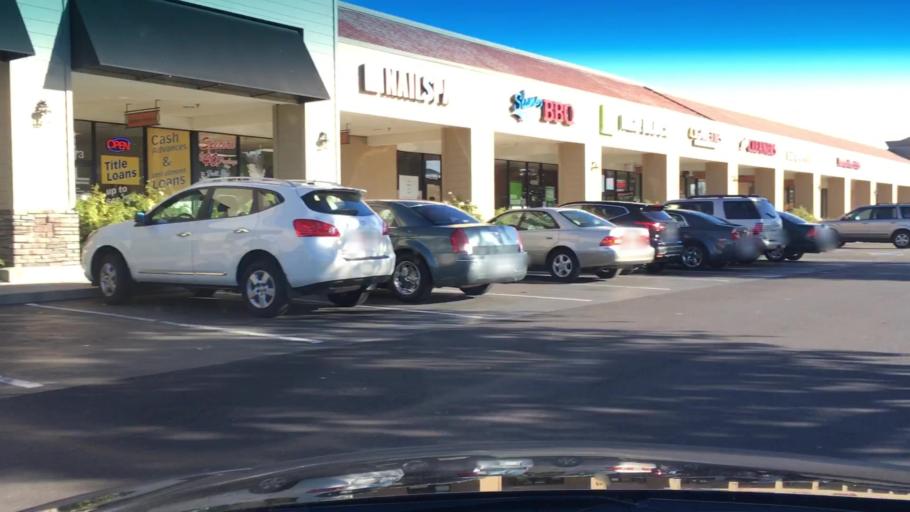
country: US
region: California
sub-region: Sacramento County
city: Parkway
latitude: 38.4752
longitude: -121.4487
